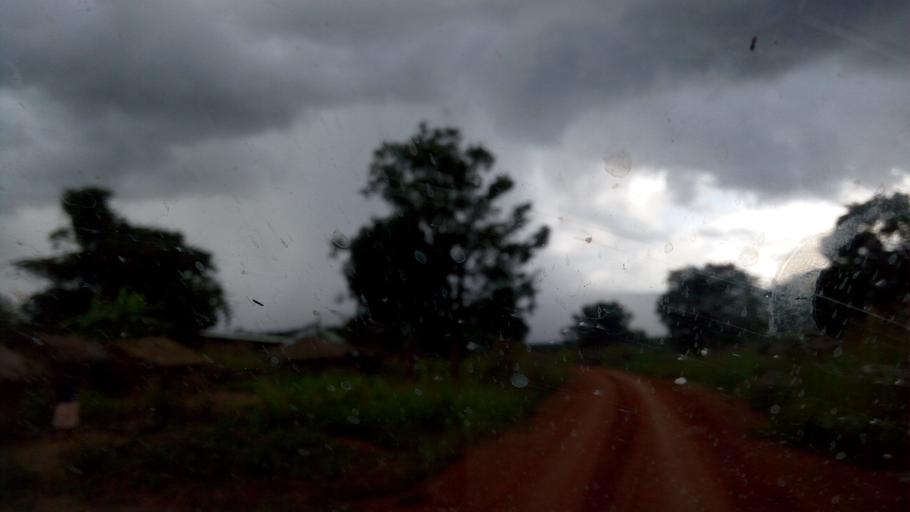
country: ZM
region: Northern
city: Kaputa
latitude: -8.0635
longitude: 29.1744
